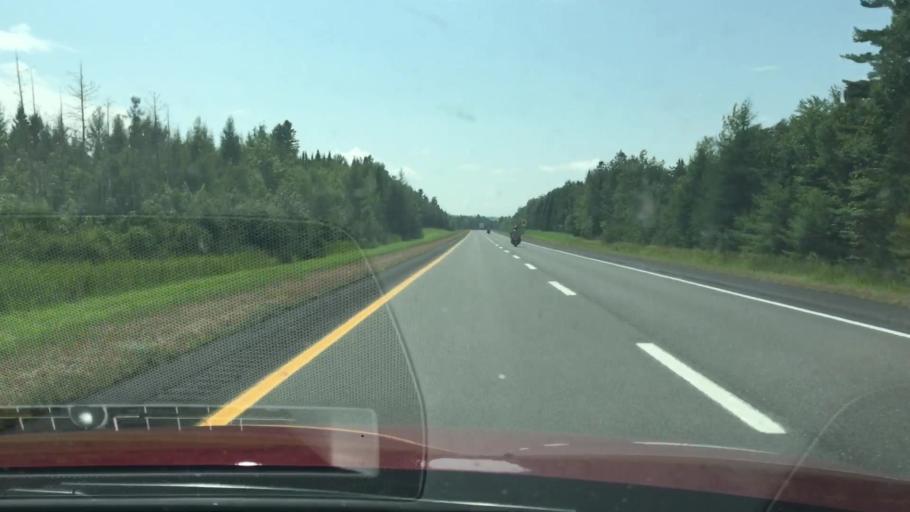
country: US
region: Maine
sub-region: Penobscot County
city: Patten
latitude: 45.9812
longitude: -68.2895
